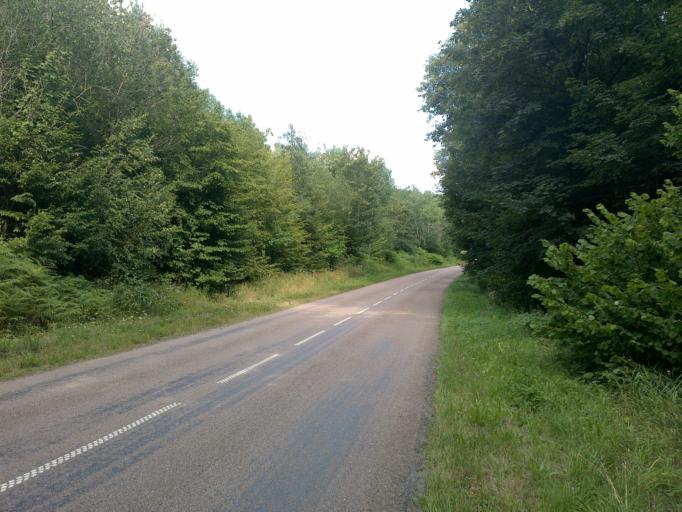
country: FR
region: Lorraine
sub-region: Departement des Vosges
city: Archettes
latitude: 48.1214
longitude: 6.5498
